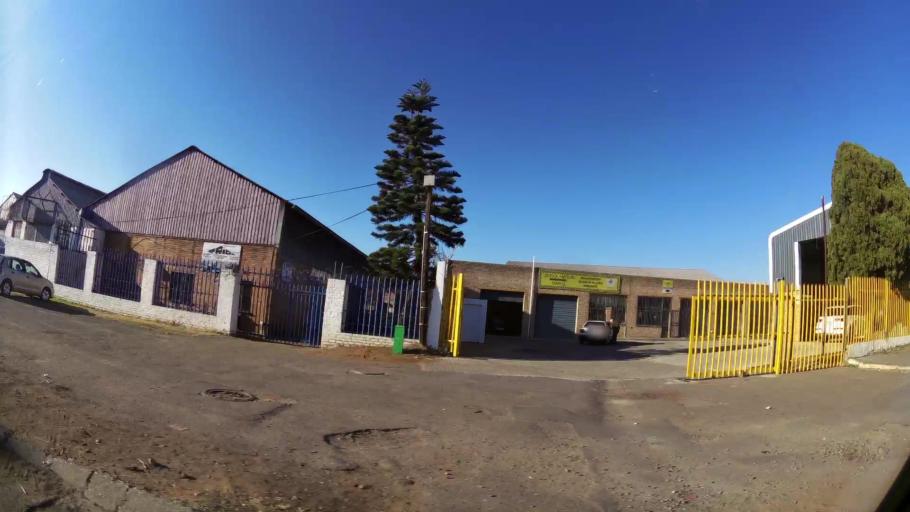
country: ZA
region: Gauteng
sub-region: City of Johannesburg Metropolitan Municipality
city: Johannesburg
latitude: -26.2073
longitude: 28.0824
